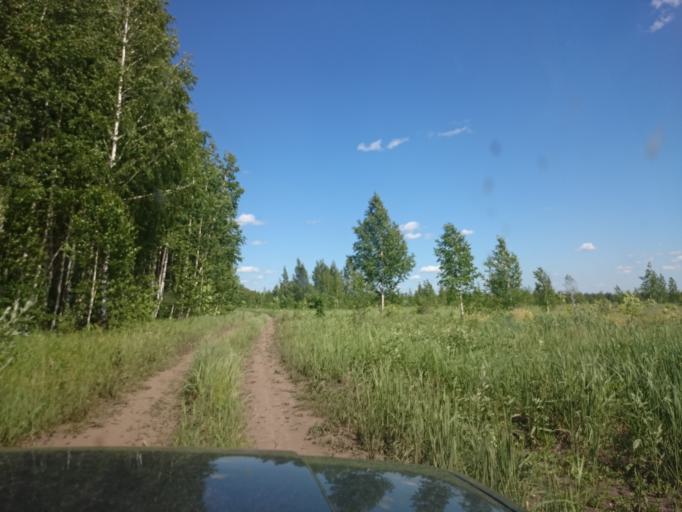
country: RU
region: Mordoviya
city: Kadoshkino
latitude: 54.0522
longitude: 44.4784
